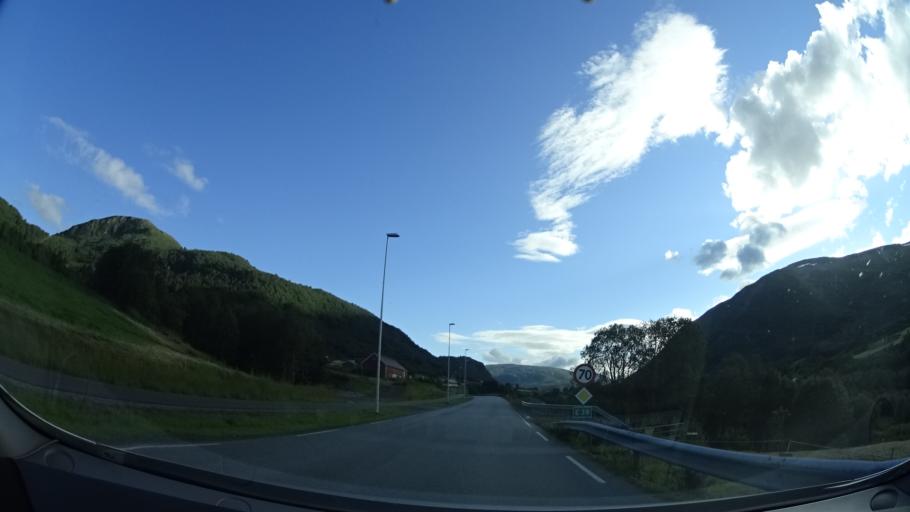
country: NO
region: More og Romsdal
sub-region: Gjemnes
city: Batnfjordsora
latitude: 62.8784
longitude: 7.6503
